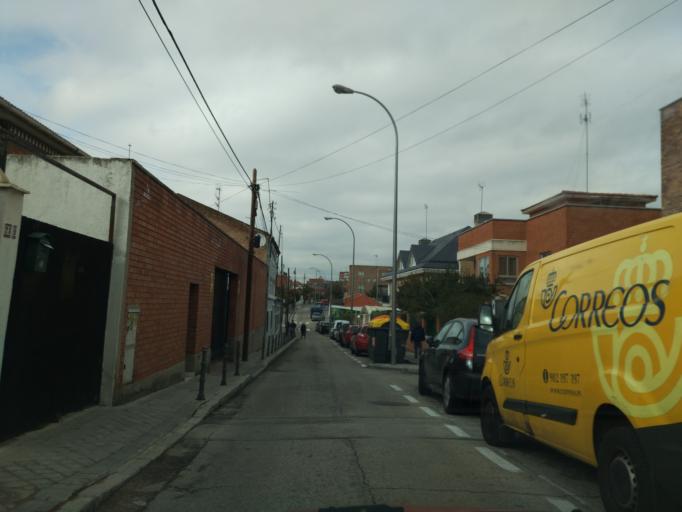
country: ES
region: Madrid
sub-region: Provincia de Madrid
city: Ciudad Lineal
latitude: 40.4645
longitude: -3.6500
